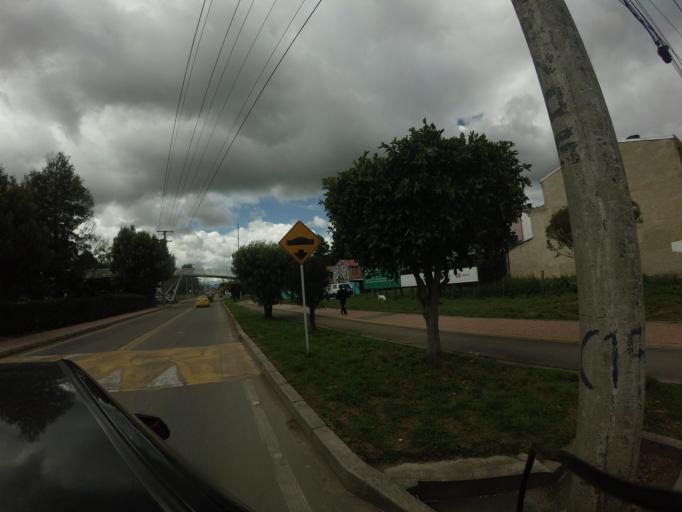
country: CO
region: Cundinamarca
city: Sopo
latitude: 4.9071
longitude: -73.9433
